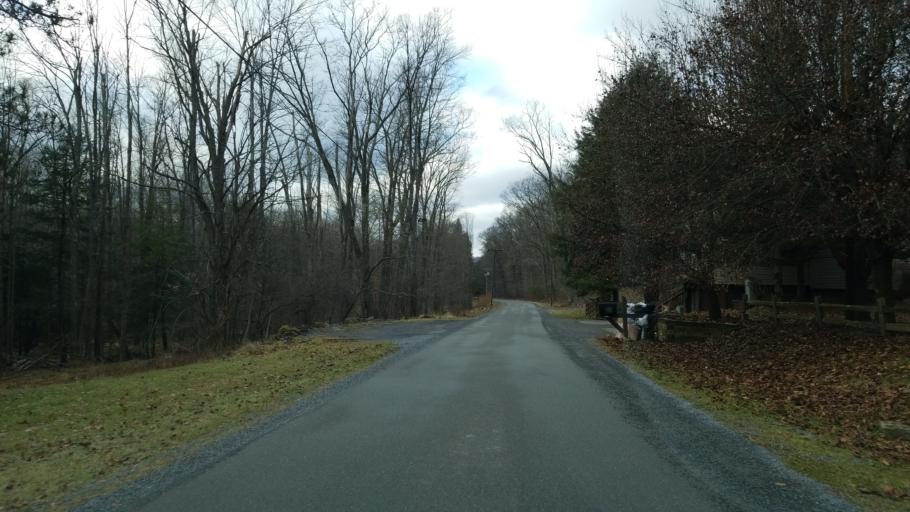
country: US
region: Pennsylvania
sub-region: Clearfield County
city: Clearfield
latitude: 41.1462
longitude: -78.5489
